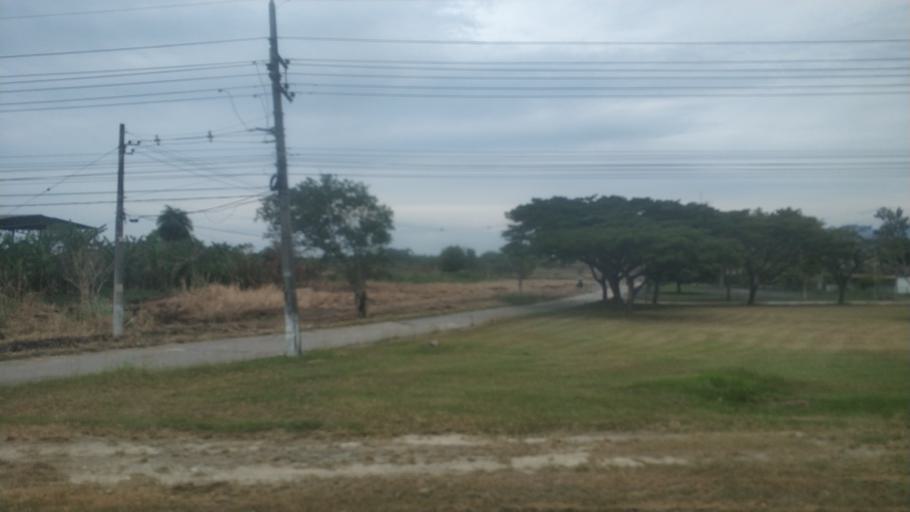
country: BR
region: Rio de Janeiro
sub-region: Seropedica
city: Seropedica
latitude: -22.7666
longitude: -43.6798
